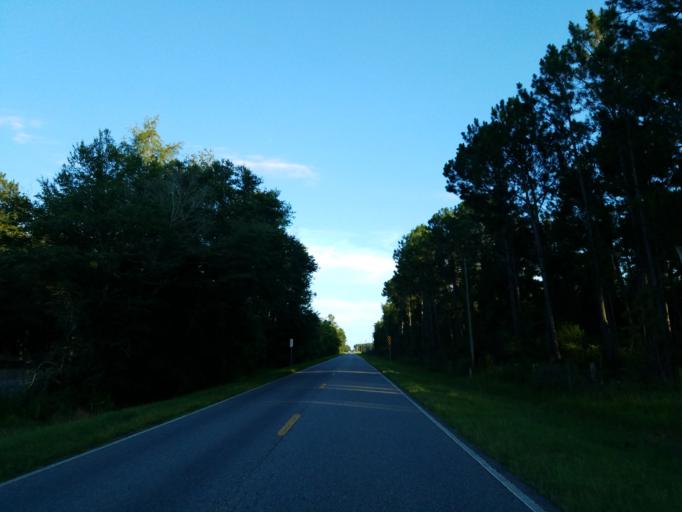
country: US
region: Georgia
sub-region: Tift County
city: Unionville
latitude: 31.3255
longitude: -83.4781
